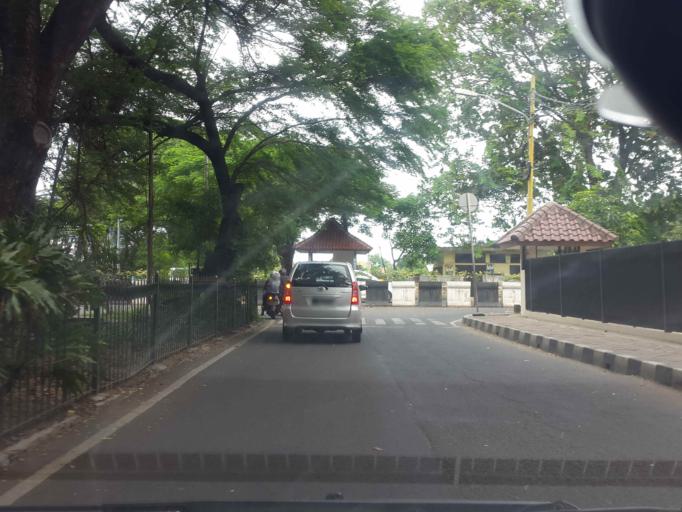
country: ID
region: Banten
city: Tangerang
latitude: -6.1695
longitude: 106.6339
